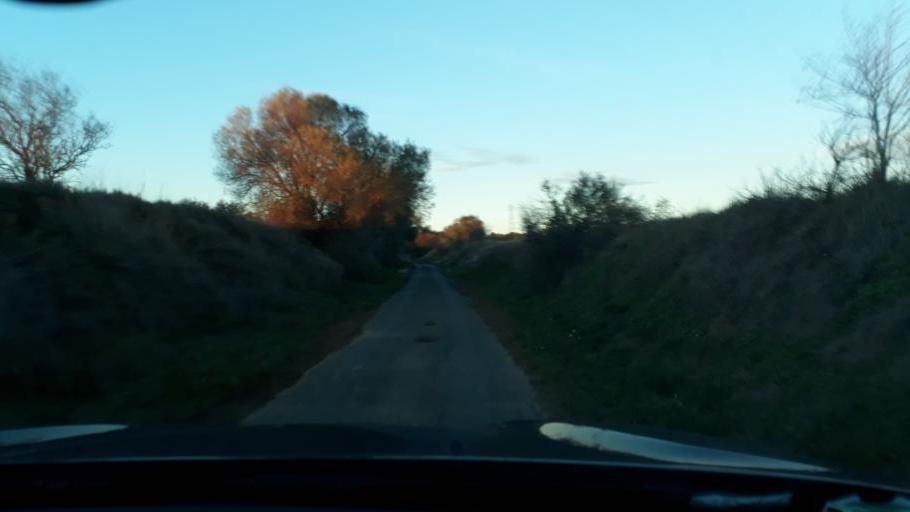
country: FR
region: Languedoc-Roussillon
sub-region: Departement de l'Herault
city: Florensac
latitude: 43.4064
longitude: 3.4602
